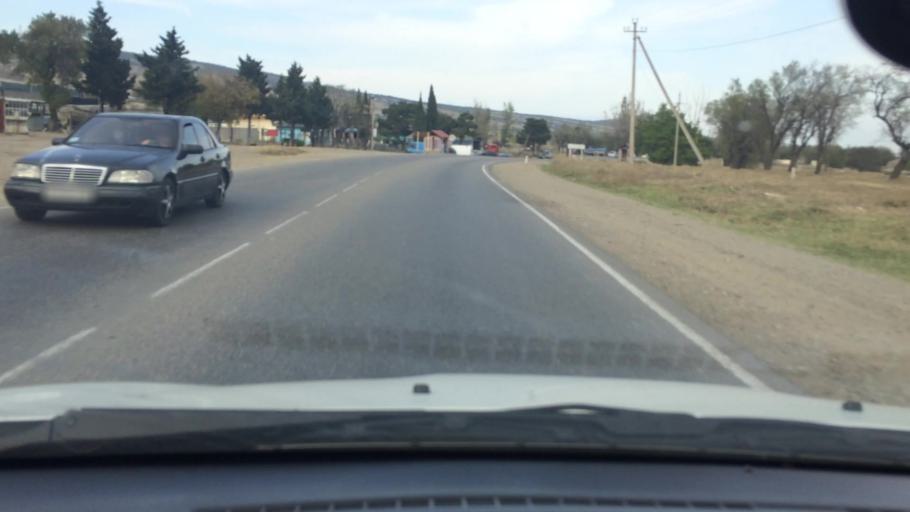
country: GE
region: T'bilisi
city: Tbilisi
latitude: 41.6286
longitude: 44.8080
